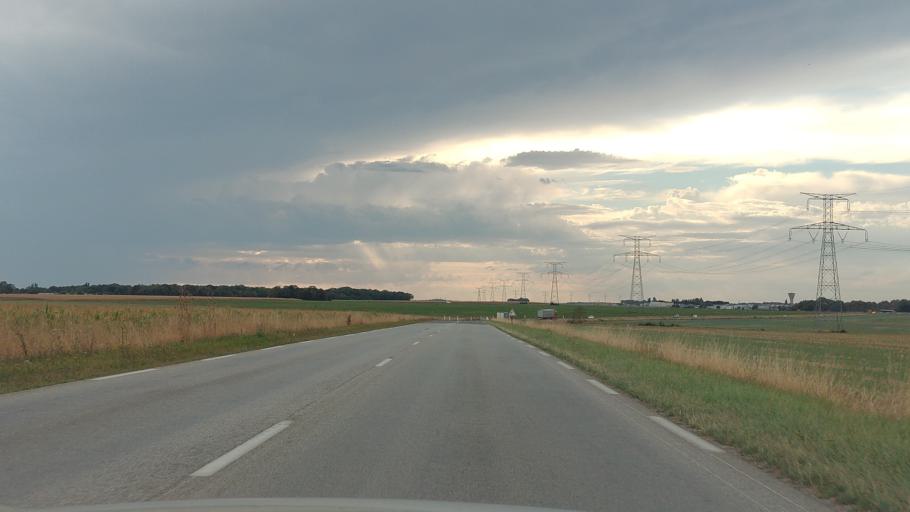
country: FR
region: Ile-de-France
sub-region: Departement de Seine-et-Marne
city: Guignes
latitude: 48.6219
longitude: 2.8362
